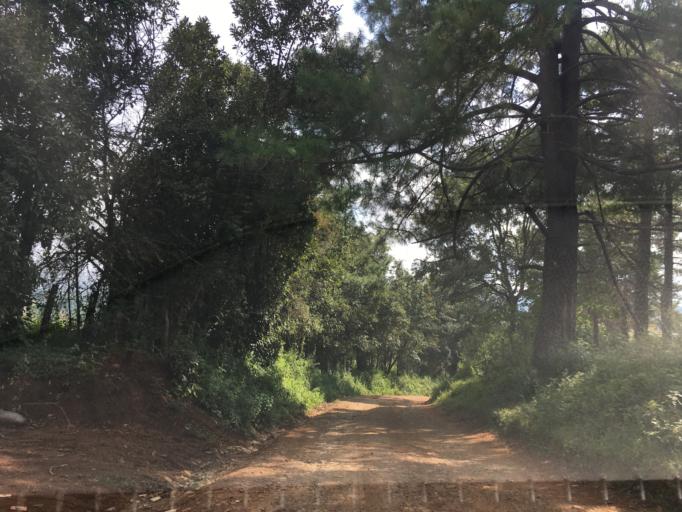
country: MX
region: Michoacan
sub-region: Morelia
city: Morelos
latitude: 19.5248
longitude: -101.2082
